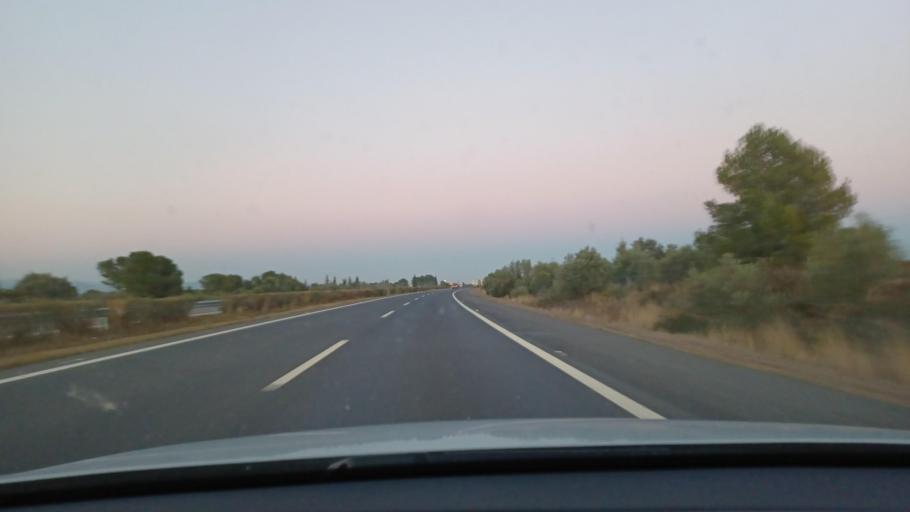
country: ES
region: Catalonia
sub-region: Provincia de Tarragona
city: Masdenverge
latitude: 40.6922
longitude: 0.5310
